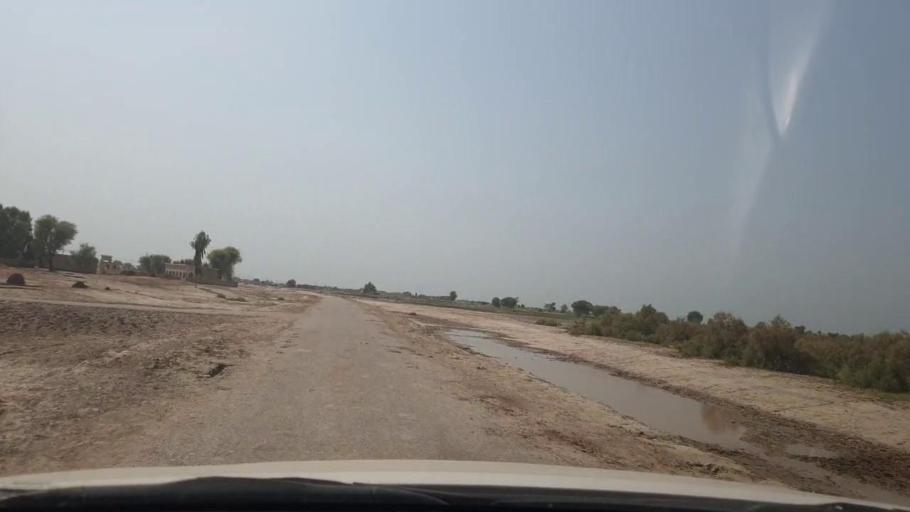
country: PK
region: Sindh
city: Shikarpur
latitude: 28.0082
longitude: 68.7093
